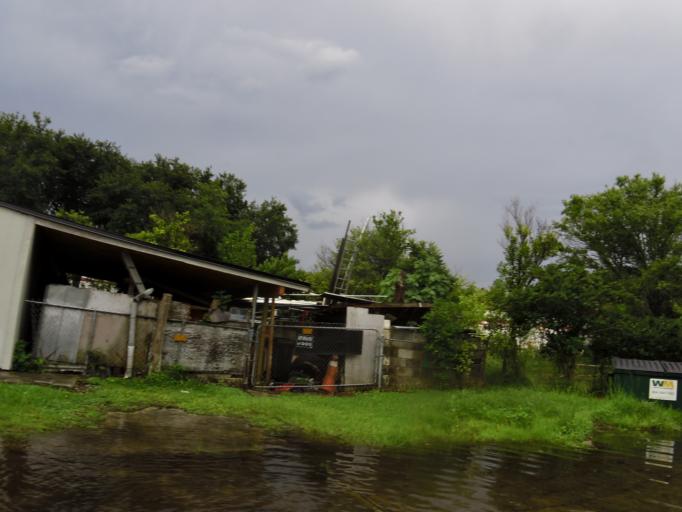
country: US
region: Florida
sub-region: Duval County
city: Jacksonville
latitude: 30.2768
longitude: -81.6267
